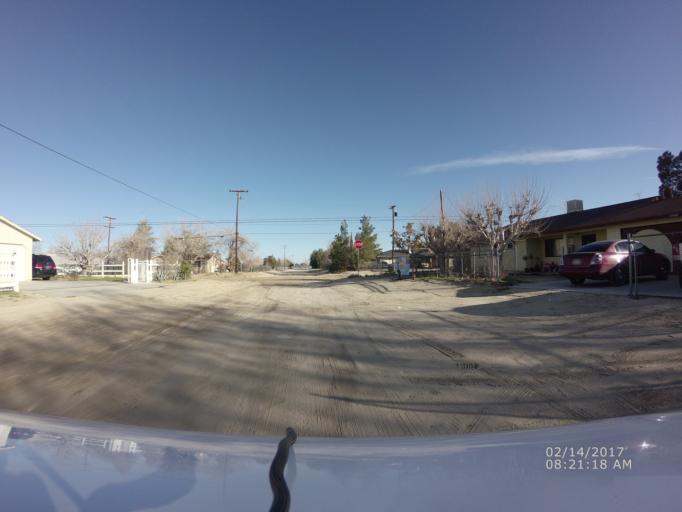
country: US
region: California
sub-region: Los Angeles County
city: Littlerock
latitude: 34.5556
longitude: -117.9538
